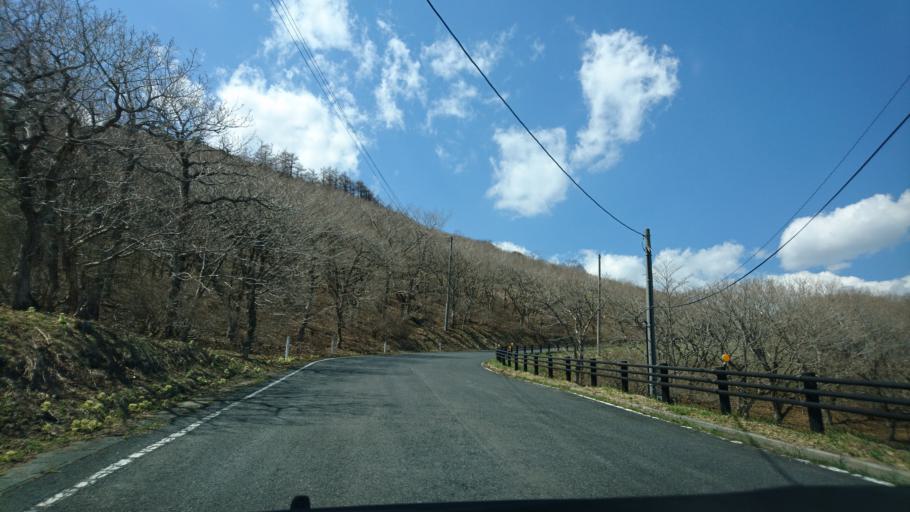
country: JP
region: Iwate
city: Ofunato
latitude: 38.9744
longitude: 141.4500
